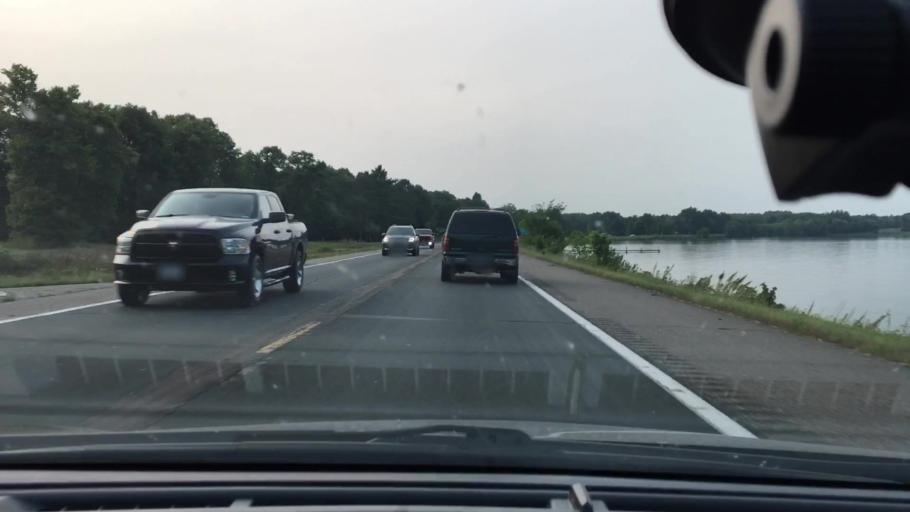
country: US
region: Minnesota
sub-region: Mille Lacs County
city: Vineland
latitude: 46.2096
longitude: -93.7900
